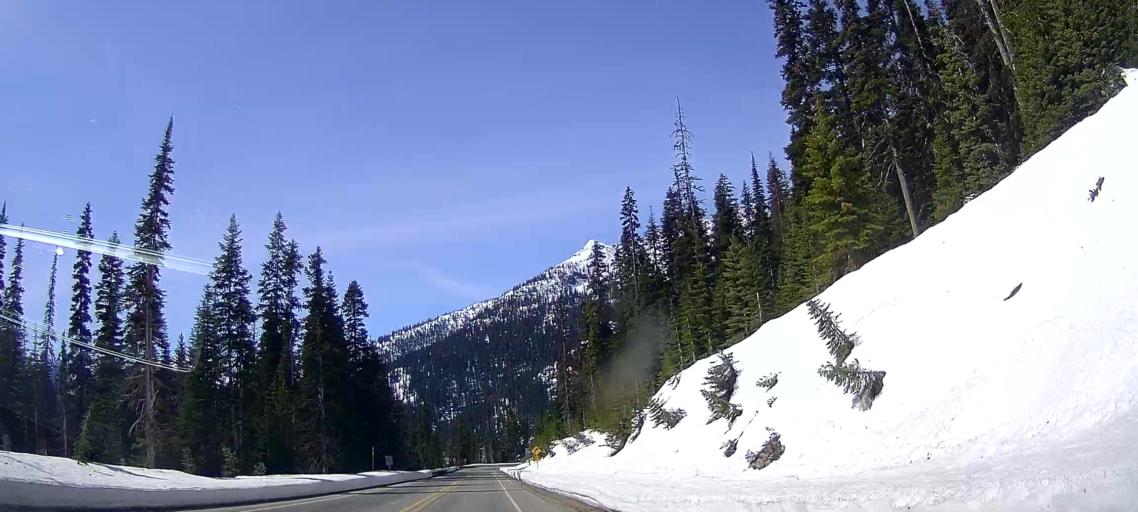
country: US
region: Washington
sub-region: Chelan County
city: Granite Falls
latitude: 48.5024
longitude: -120.7044
